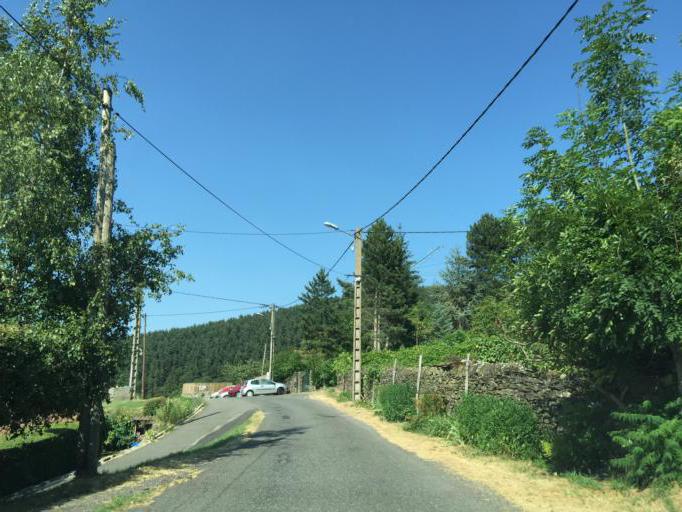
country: FR
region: Rhone-Alpes
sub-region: Departement de la Loire
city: Saint-Jean-Bonnefonds
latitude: 45.4330
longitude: 4.4869
